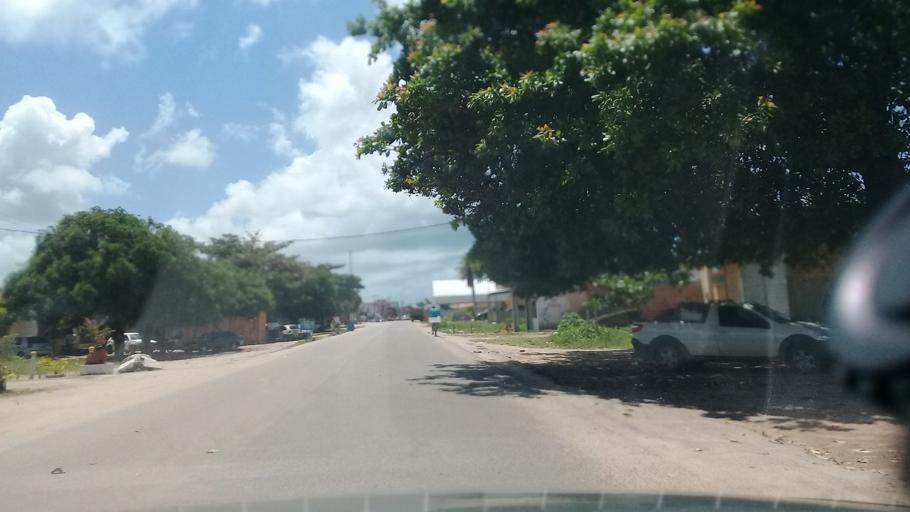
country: BR
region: Pernambuco
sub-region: Sirinhaem
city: Sirinhaem
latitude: -8.6134
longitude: -35.0542
